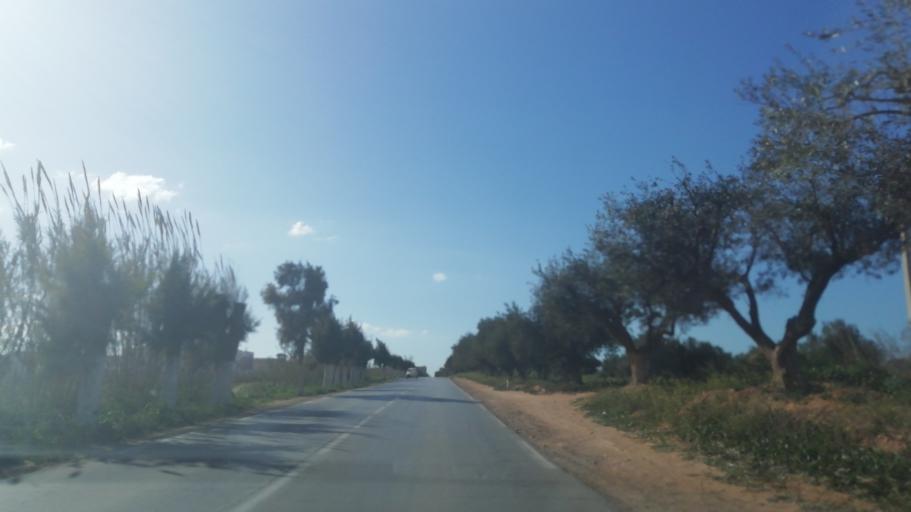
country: DZ
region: Mostaganem
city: Mostaganem
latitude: 35.9989
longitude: 0.3150
